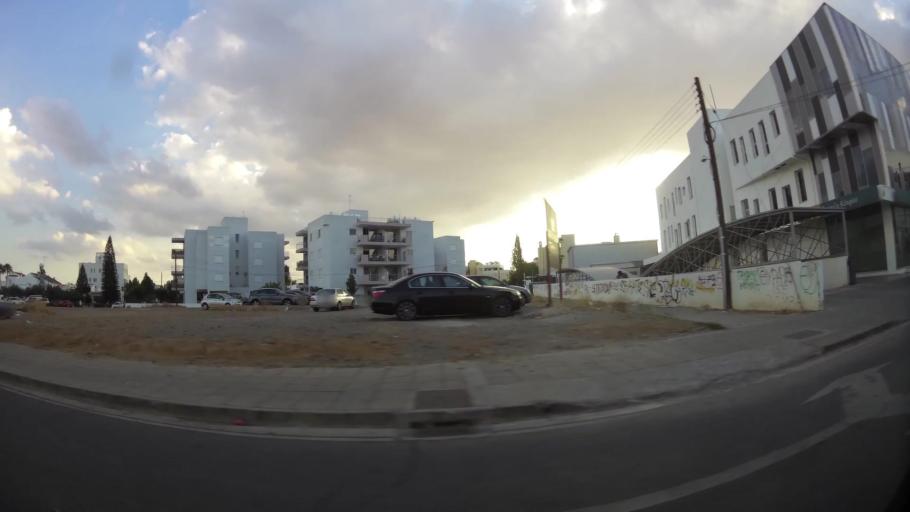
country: CY
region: Lefkosia
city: Tseri
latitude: 35.1224
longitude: 33.3210
